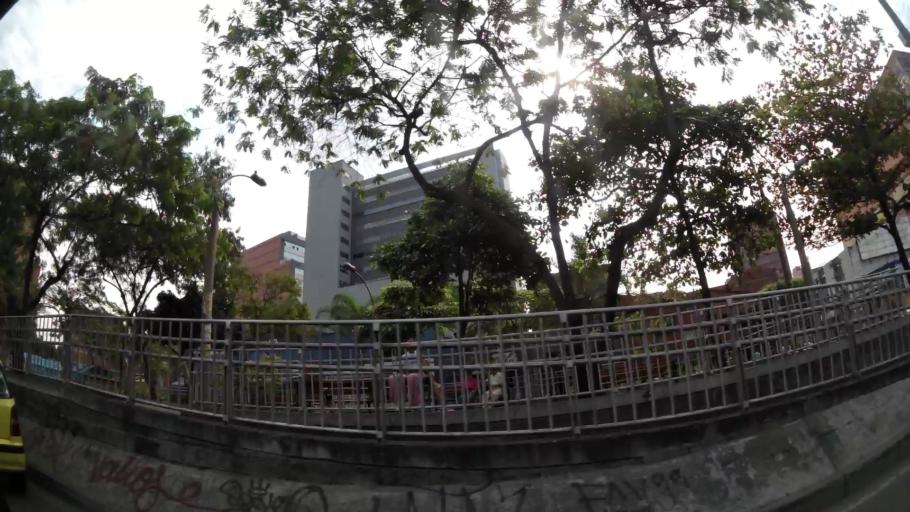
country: CO
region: Antioquia
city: Medellin
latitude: 6.2504
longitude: -75.5749
